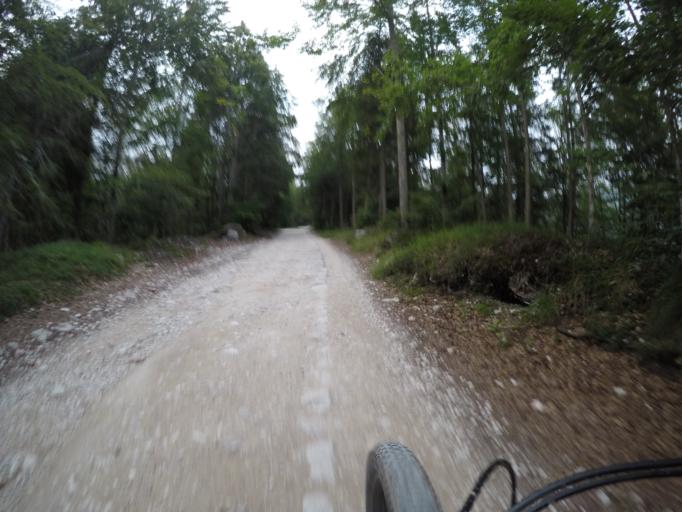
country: IT
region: Veneto
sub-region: Provincia di Vicenza
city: Gallio
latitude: 45.9060
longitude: 11.5248
